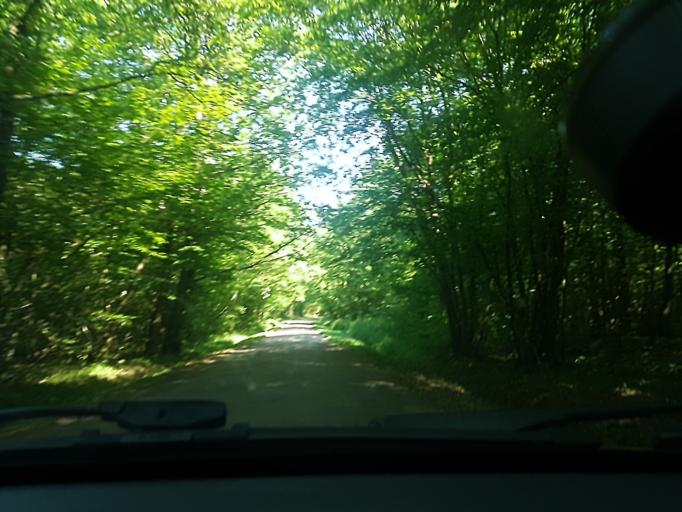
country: FR
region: Bourgogne
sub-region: Departement de Saone-et-Loire
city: Demigny
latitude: 46.8865
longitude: 4.8128
